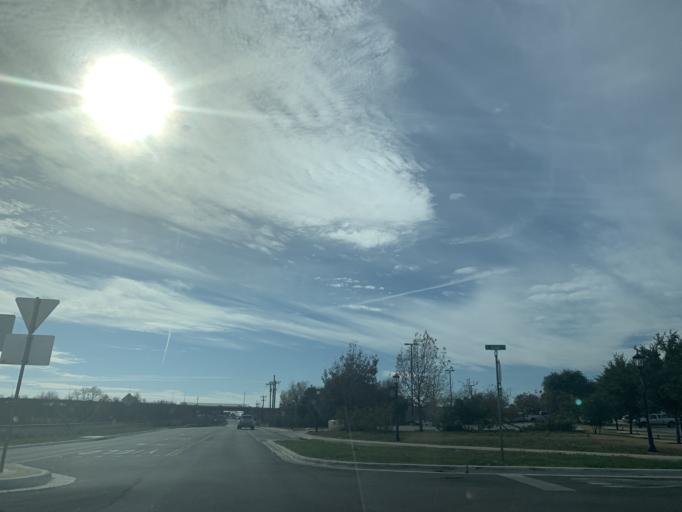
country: US
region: Texas
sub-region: Williamson County
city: Round Rock
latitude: 30.5063
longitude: -97.6789
